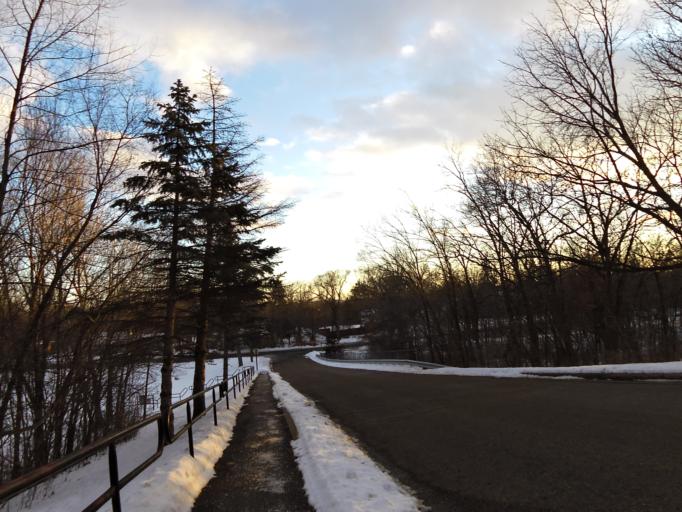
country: US
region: Wisconsin
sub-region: Saint Croix County
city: Hudson
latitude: 44.9714
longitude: -92.7515
